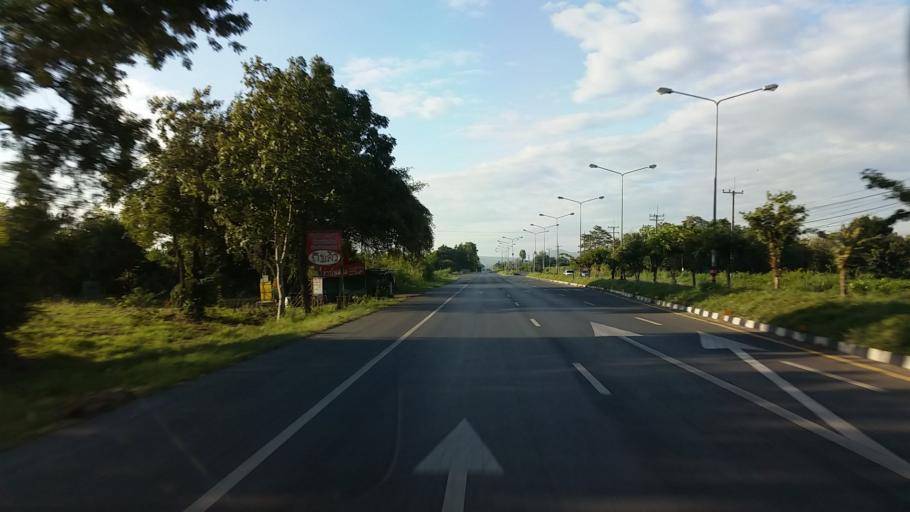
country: TH
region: Lop Buri
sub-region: Amphoe Tha Luang
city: Tha Luang
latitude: 15.0320
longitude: 100.9524
